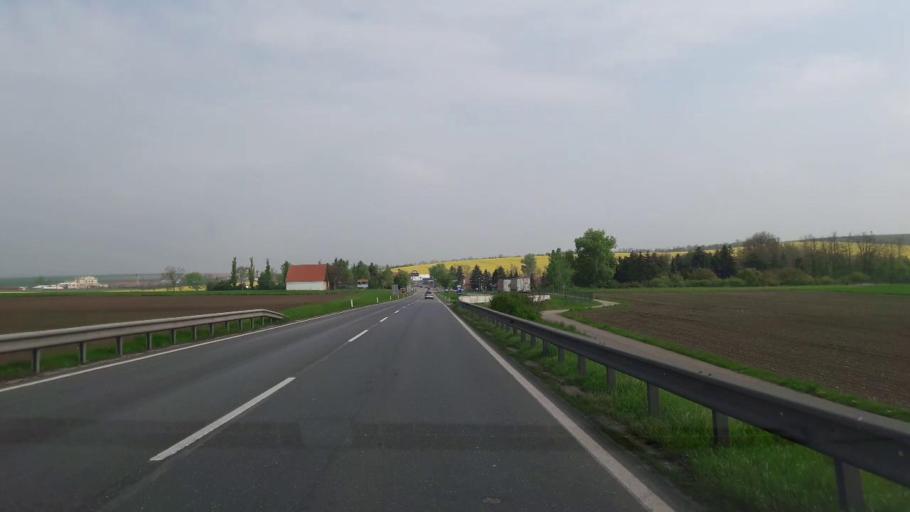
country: AT
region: Lower Austria
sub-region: Politischer Bezirk Hollabrunn
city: Haugsdorf
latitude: 48.7497
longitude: 16.0630
